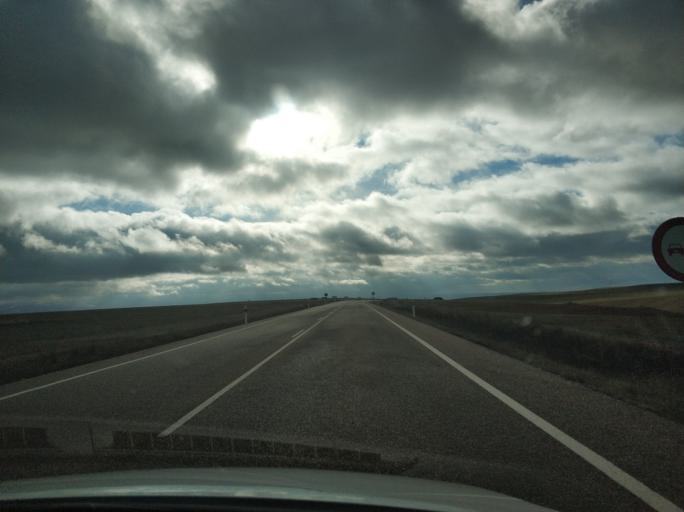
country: ES
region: Castille and Leon
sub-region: Provincia de Soria
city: Fuentecambron
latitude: 41.4599
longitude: -3.3325
